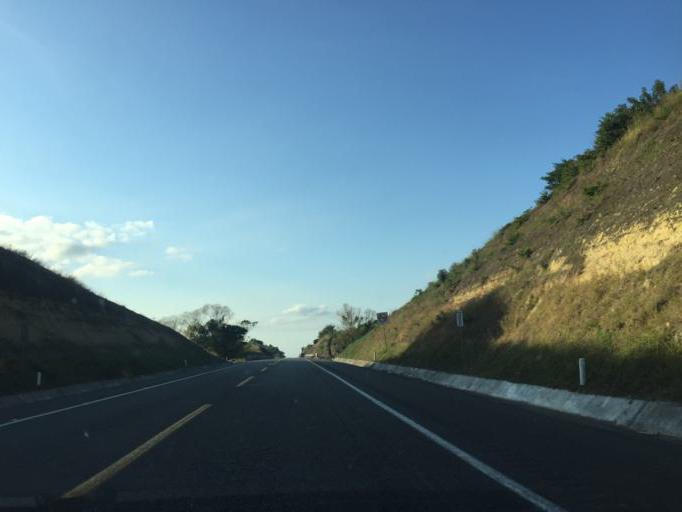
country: MX
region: Veracruz
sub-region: Papantla
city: Residencial Tajin
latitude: 20.5965
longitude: -97.3748
